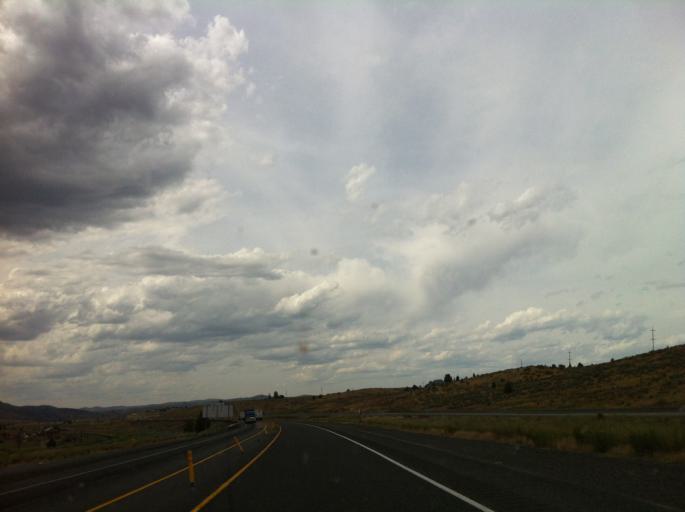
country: US
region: Oregon
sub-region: Baker County
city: Baker City
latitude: 44.5540
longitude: -117.4247
